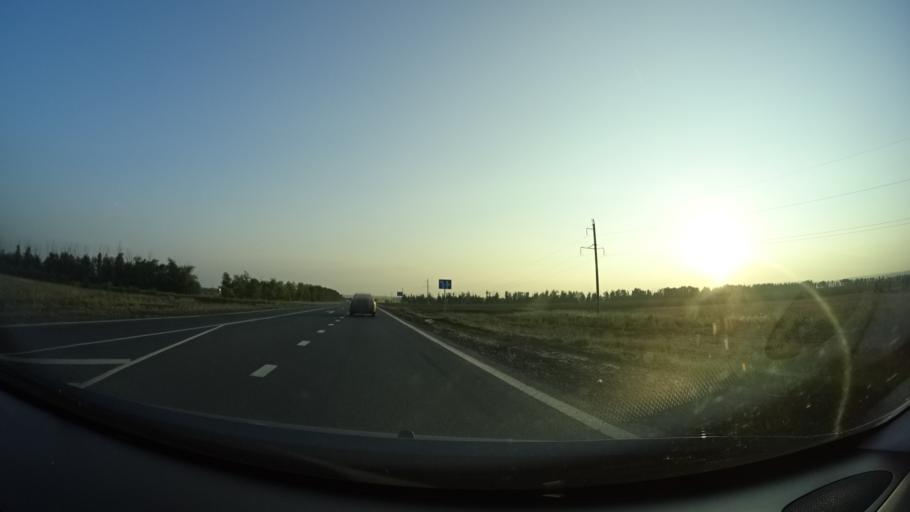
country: RU
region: Samara
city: Sernovodsk
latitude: 53.9580
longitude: 51.4021
